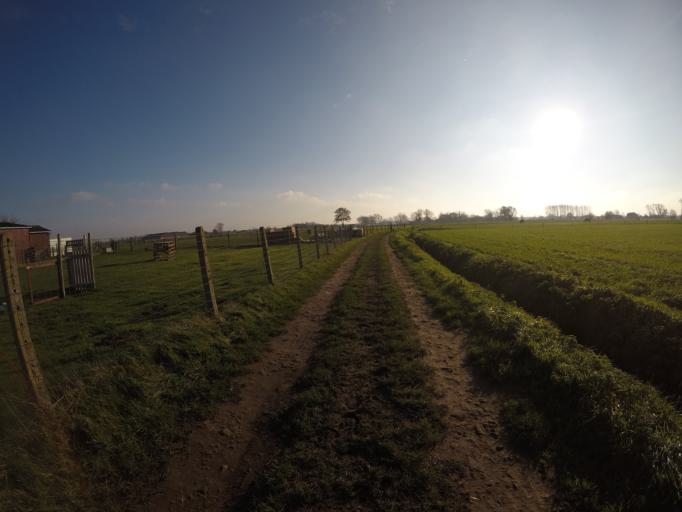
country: BE
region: Flanders
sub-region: Provincie West-Vlaanderen
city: Lichtervelde
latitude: 51.0637
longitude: 3.1921
